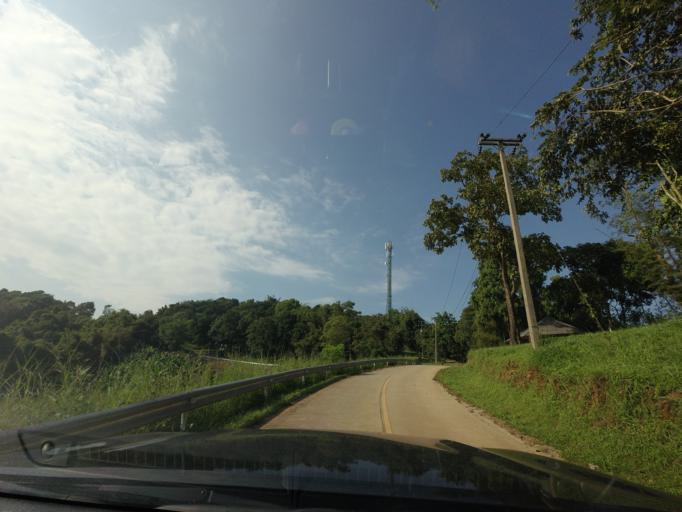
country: TH
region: Nan
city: Na Noi
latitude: 18.3738
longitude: 100.8280
